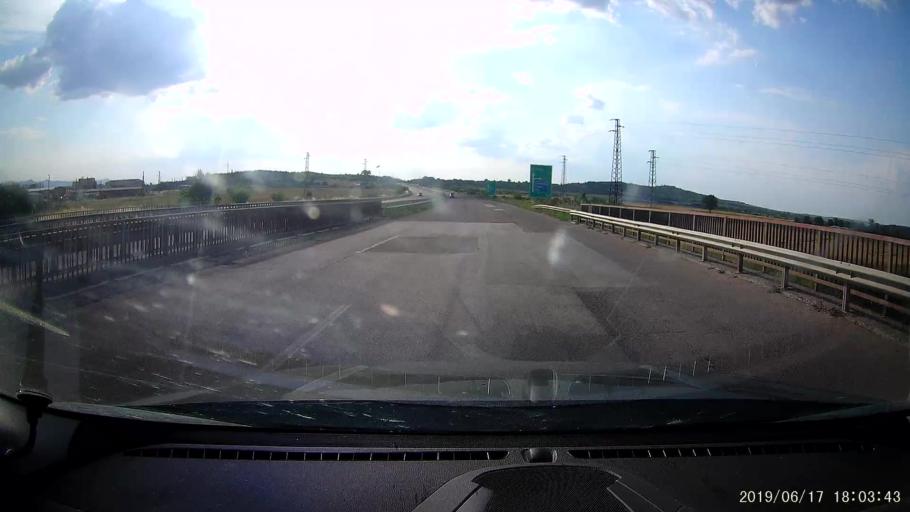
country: BG
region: Khaskovo
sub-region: Obshtina Svilengrad
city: Svilengrad
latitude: 41.7805
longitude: 26.2139
